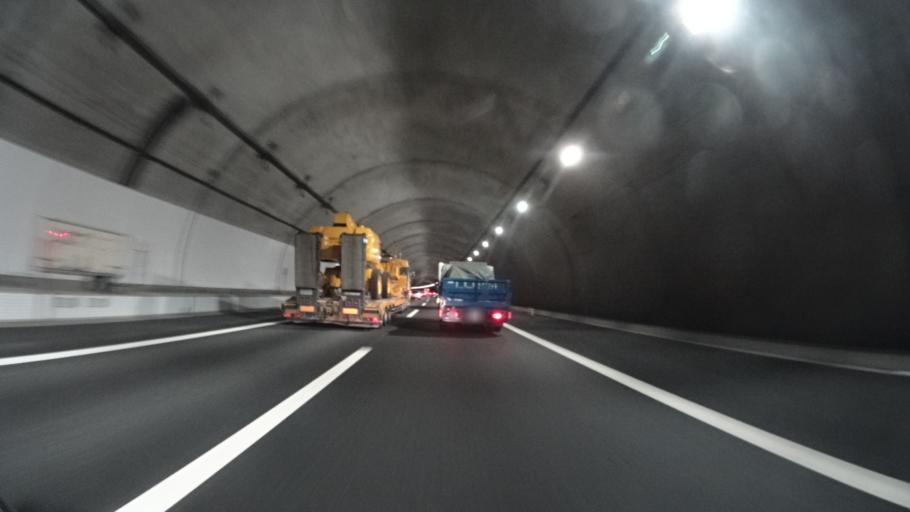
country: JP
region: Shiga Prefecture
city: Kusatsu
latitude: 34.9490
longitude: 136.0197
